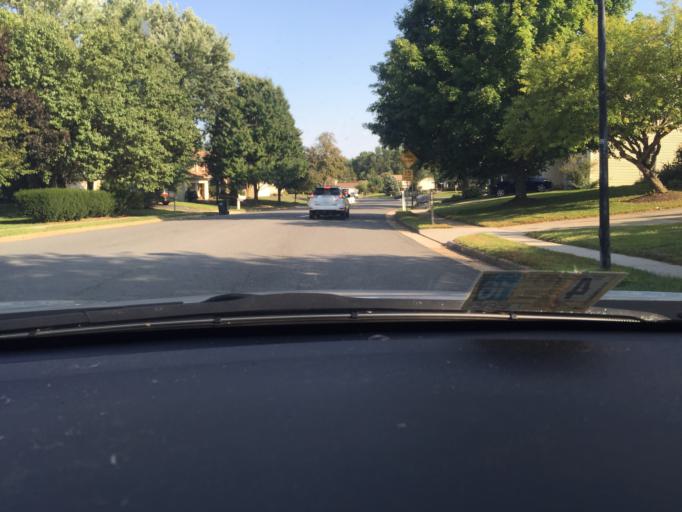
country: US
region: Virginia
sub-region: Fairfax County
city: Oak Hill
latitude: 38.9164
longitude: -77.4171
